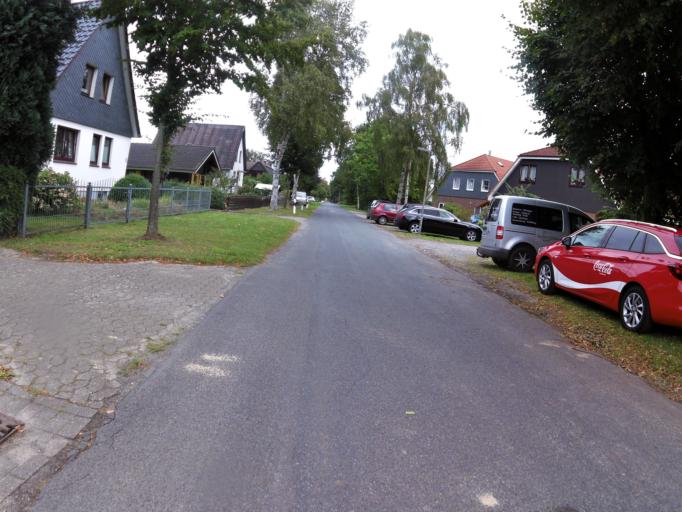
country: DE
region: Lower Saxony
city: Kuhrstedt
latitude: 53.5043
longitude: 8.7893
